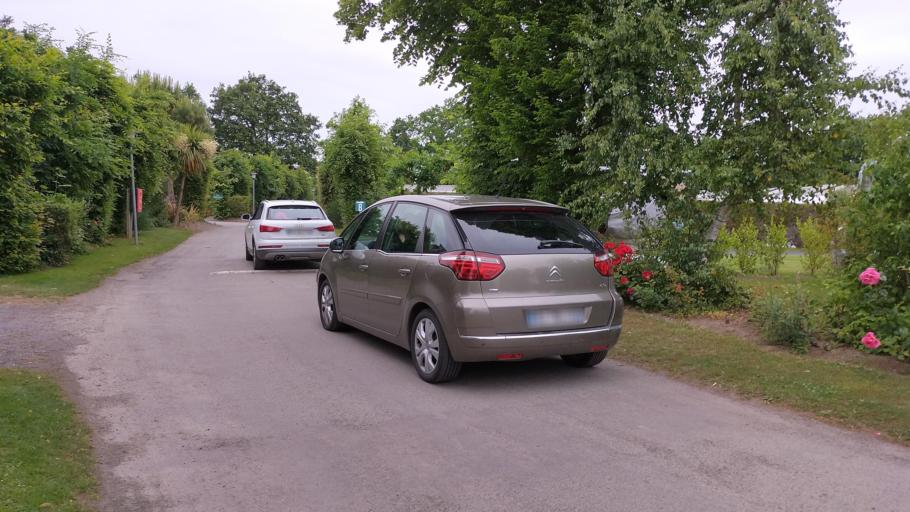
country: FR
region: Brittany
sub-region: Departement d'Ille-et-Vilaine
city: Saint-Jouan-des-Guerets
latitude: 48.6109
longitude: -1.9873
